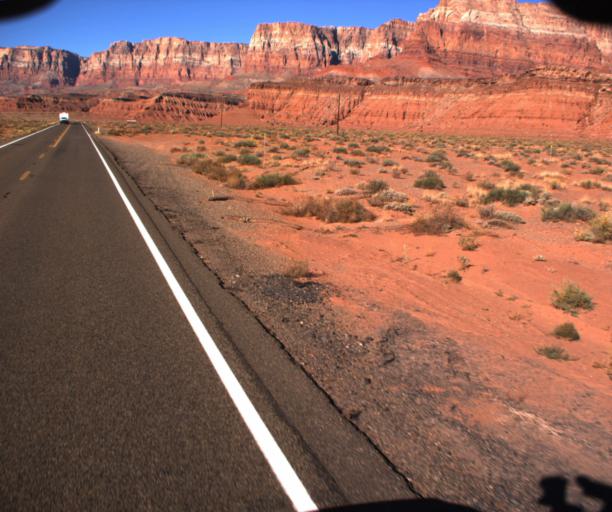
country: US
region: Arizona
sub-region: Coconino County
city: Page
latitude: 36.8153
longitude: -111.6424
